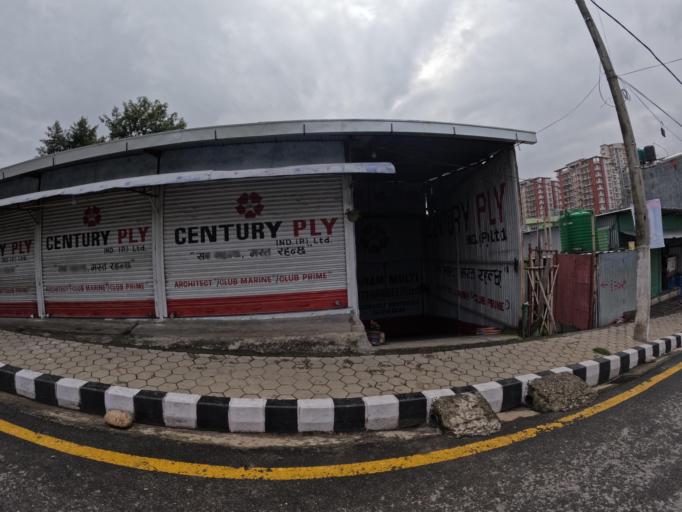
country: NP
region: Central Region
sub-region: Bagmati Zone
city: Kathmandu
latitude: 27.7563
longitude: 85.3249
